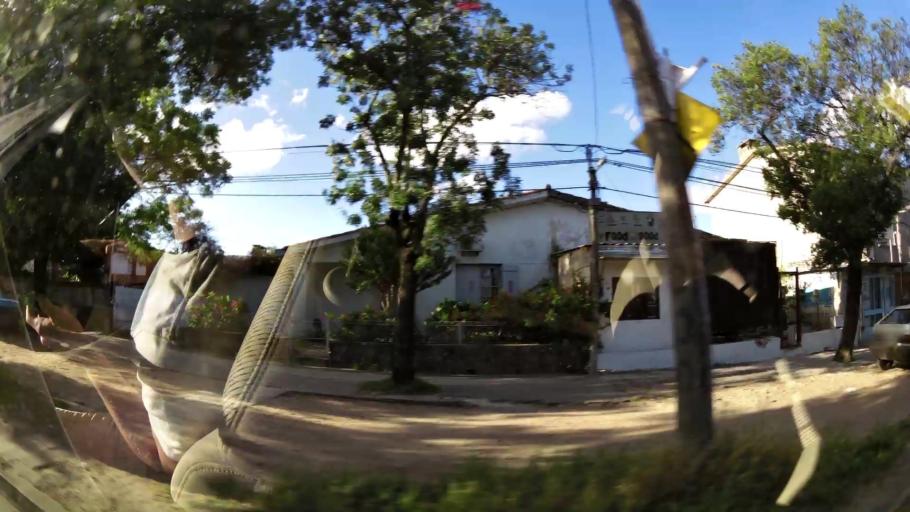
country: UY
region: Montevideo
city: Montevideo
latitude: -34.8744
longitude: -56.2531
